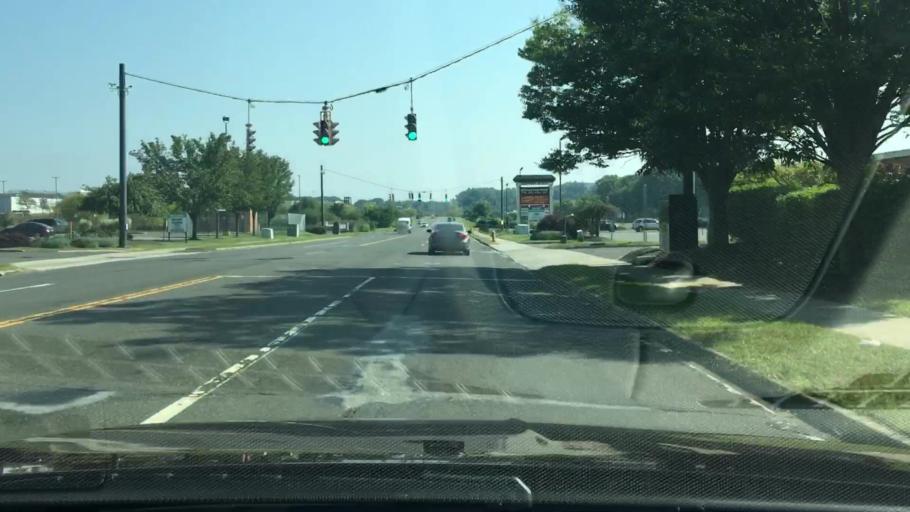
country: US
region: Connecticut
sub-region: Fairfield County
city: Danbury
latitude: 41.3753
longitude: -73.4865
